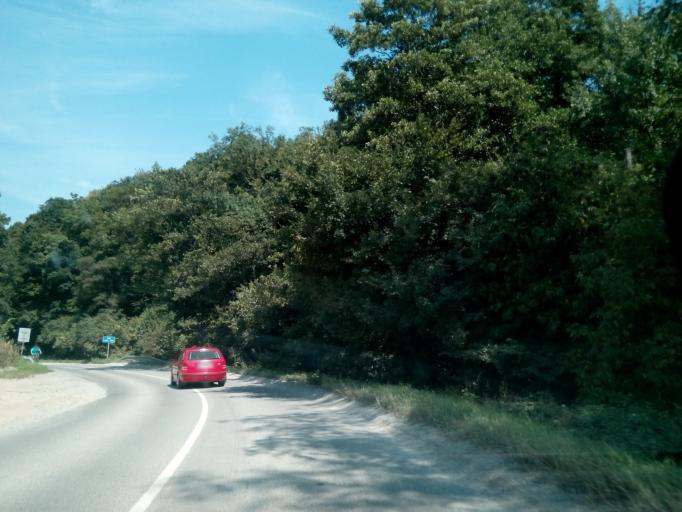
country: SK
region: Kosicky
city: Kosice
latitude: 48.7711
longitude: 21.2428
